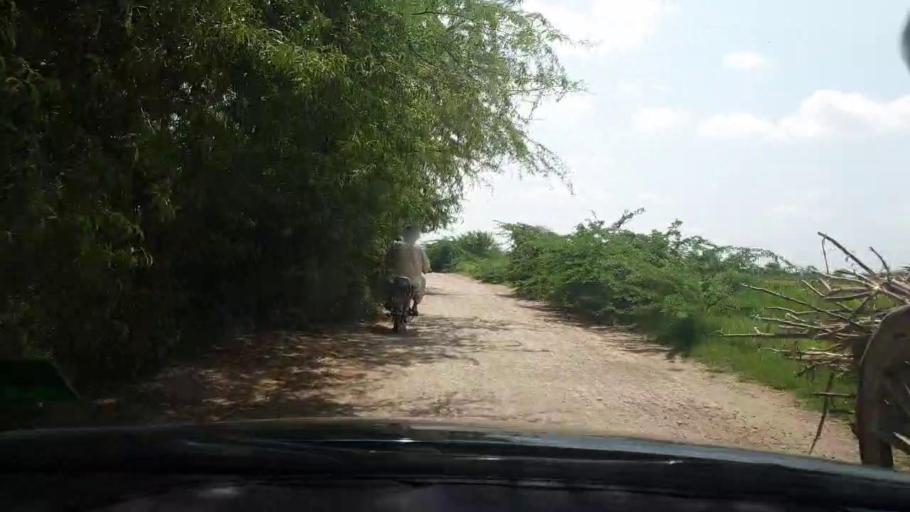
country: PK
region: Sindh
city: Tando Bago
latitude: 24.8790
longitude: 69.0805
